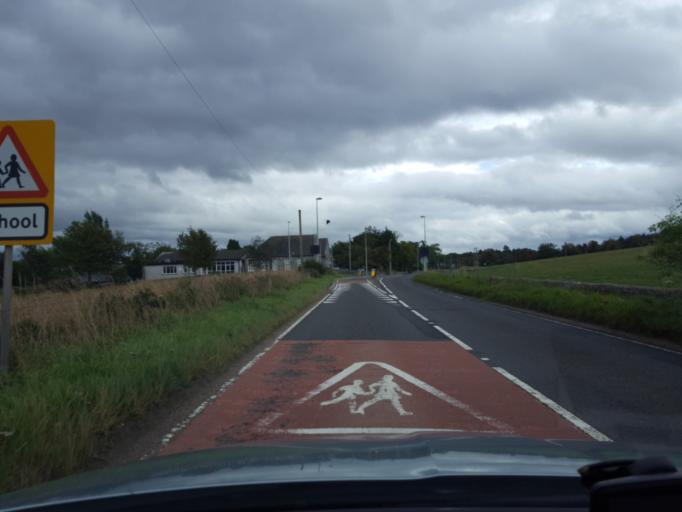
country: GB
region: Scotland
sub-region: Aberdeenshire
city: Kemnay
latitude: 57.1739
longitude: -2.4207
